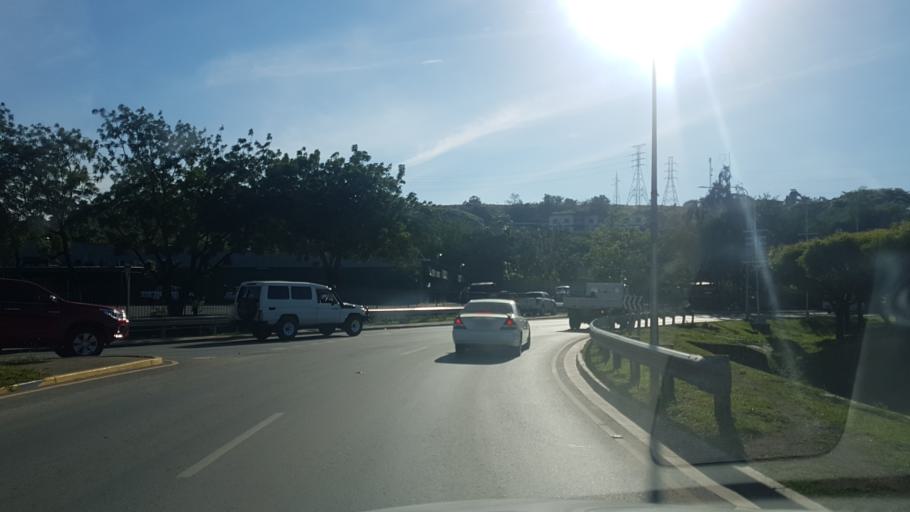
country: PG
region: National Capital
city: Port Moresby
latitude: -9.4503
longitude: 147.1957
